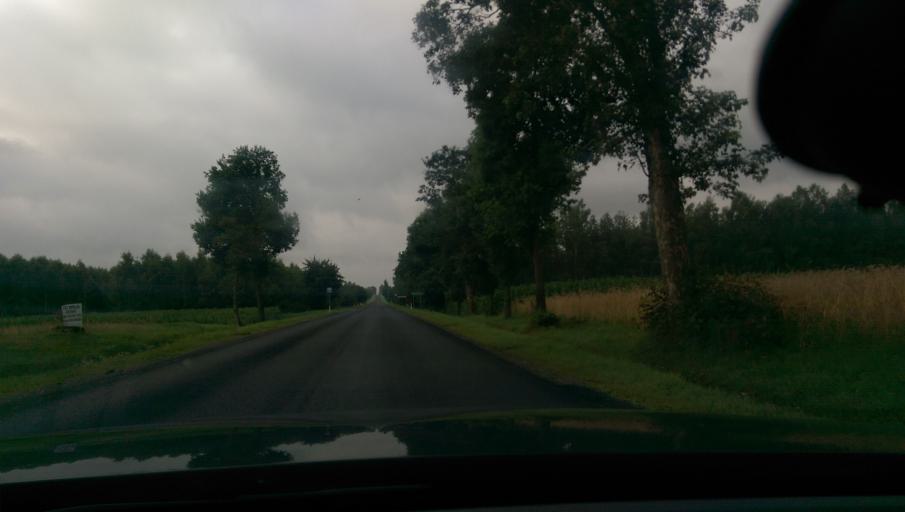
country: PL
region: Masovian Voivodeship
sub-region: Powiat przasnyski
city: Przasnysz
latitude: 53.0959
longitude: 20.8544
